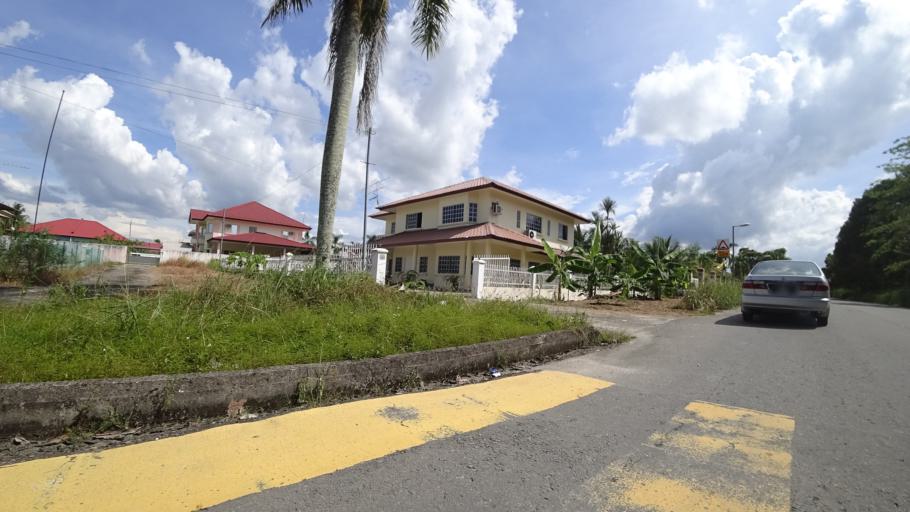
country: BN
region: Brunei and Muara
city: Bandar Seri Begawan
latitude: 4.8726
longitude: 114.8533
